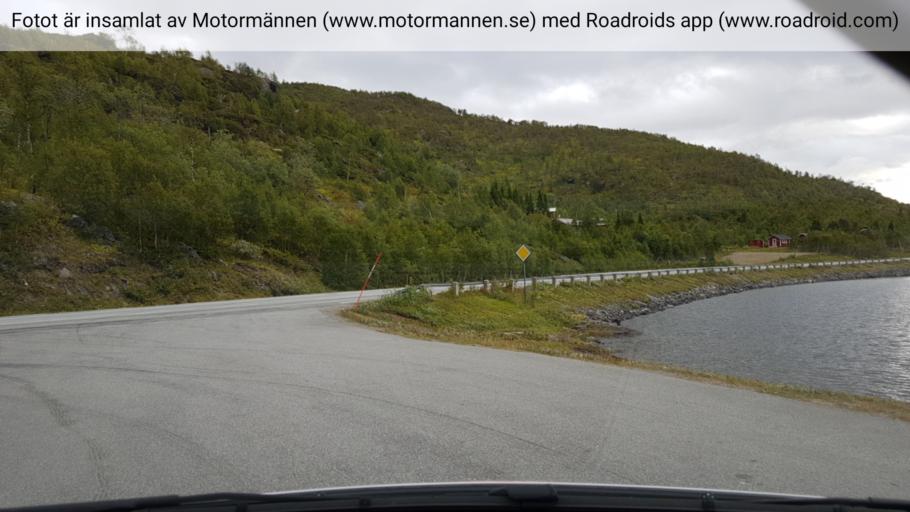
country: NO
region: Nordland
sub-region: Rana
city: Mo i Rana
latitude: 66.1348
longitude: 14.5922
